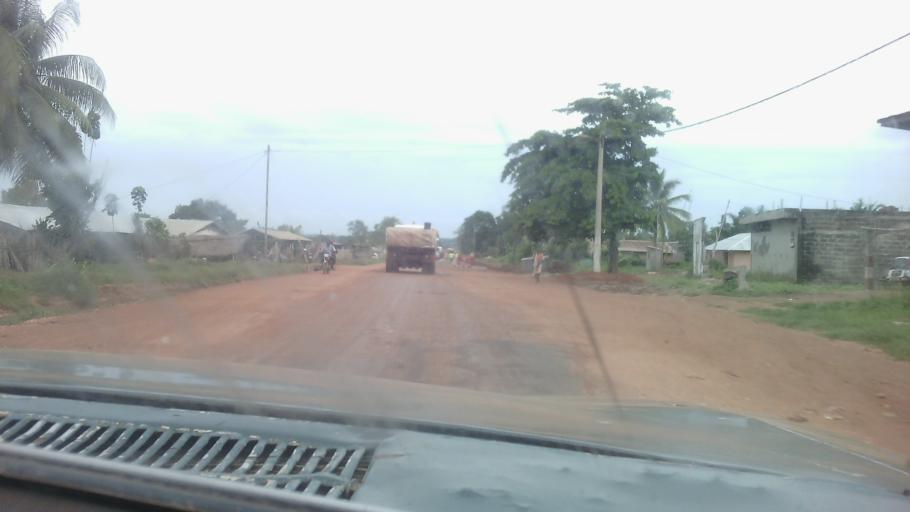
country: BJ
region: Mono
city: Lokossa
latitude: 6.5557
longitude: 1.8172
